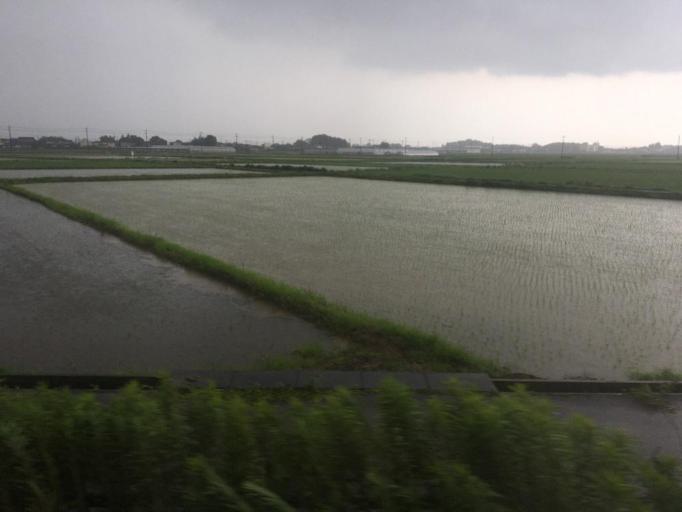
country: JP
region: Gunma
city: Tatebayashi
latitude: 36.2826
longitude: 139.4856
